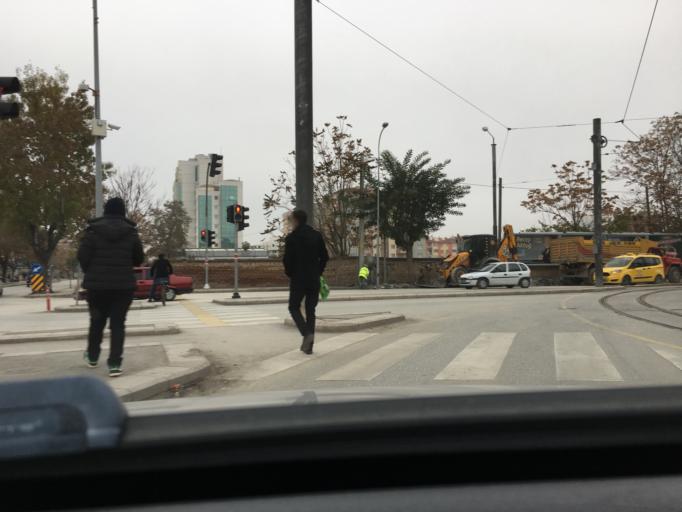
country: TR
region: Eskisehir
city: Eskisehir
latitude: 39.7816
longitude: 30.5091
